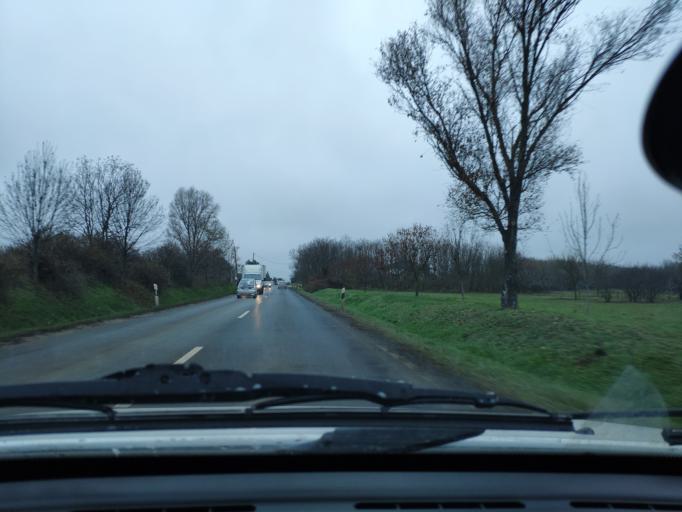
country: HU
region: Pest
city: Soskut
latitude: 47.3969
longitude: 18.8426
